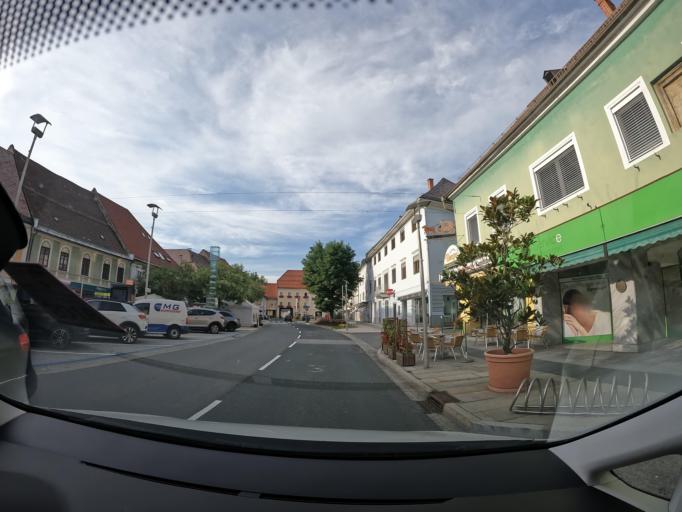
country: AT
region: Carinthia
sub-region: Politischer Bezirk Volkermarkt
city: Voelkermarkt
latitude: 46.6593
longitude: 14.6344
